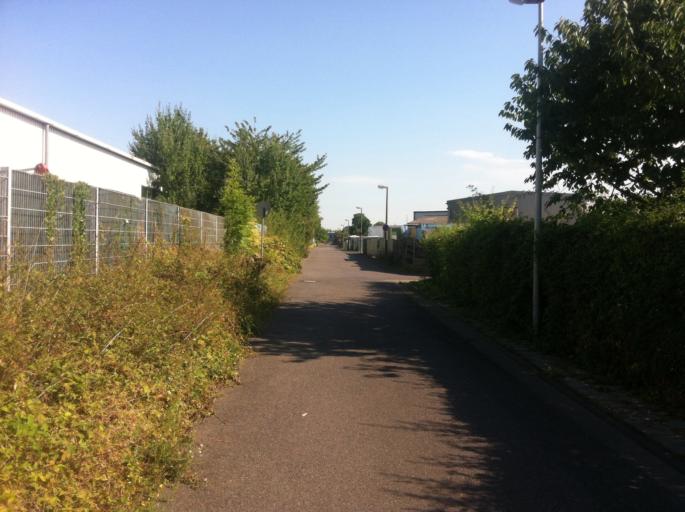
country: DE
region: North Rhine-Westphalia
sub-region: Regierungsbezirk Koln
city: Pulheim
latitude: 50.9656
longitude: 6.8127
